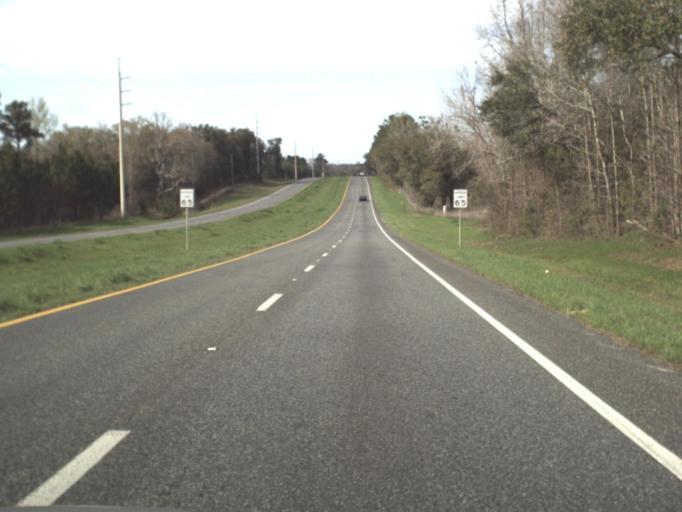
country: US
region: Florida
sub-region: Jefferson County
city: Monticello
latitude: 30.4205
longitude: -83.9109
